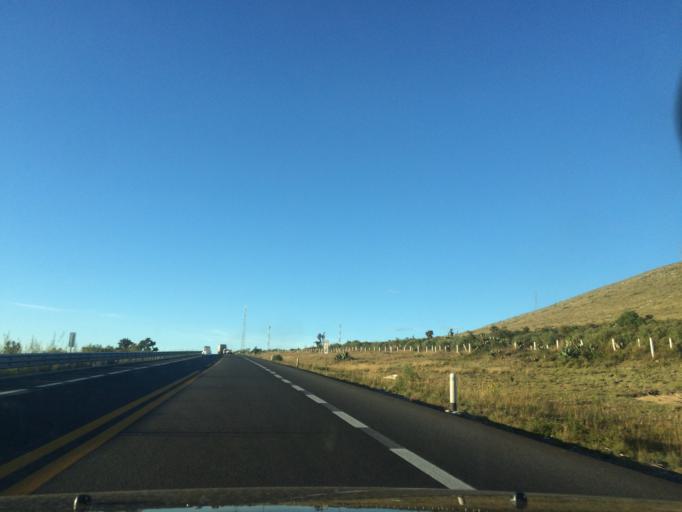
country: MX
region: Puebla
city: Morelos Canada
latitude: 18.7217
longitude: -97.4728
